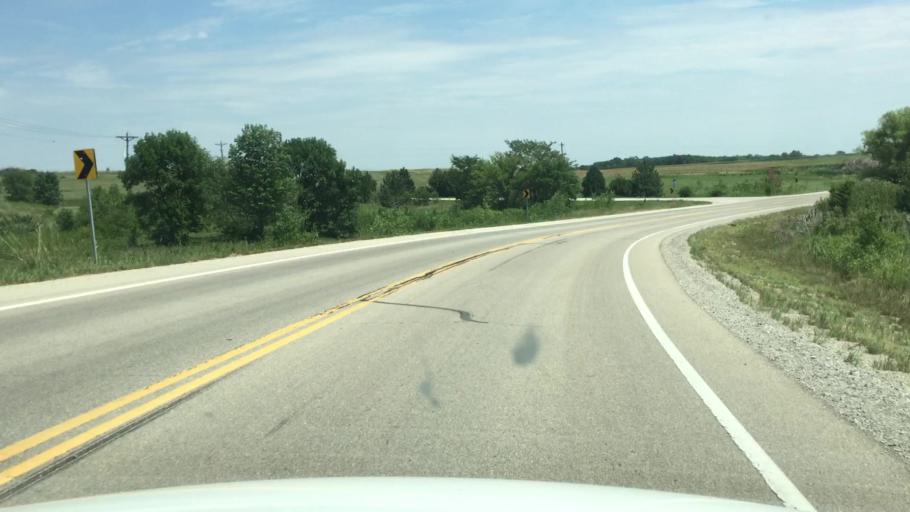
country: US
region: Kansas
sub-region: Shawnee County
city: Topeka
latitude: 38.9858
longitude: -95.4938
